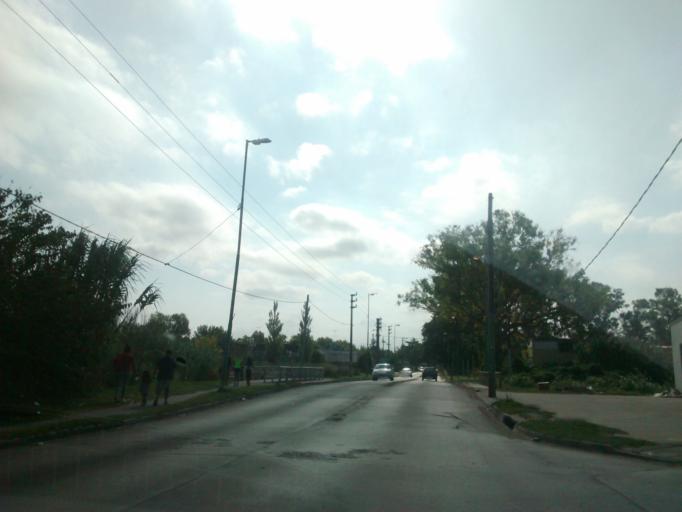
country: AR
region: Buenos Aires
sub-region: Partido de La Plata
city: La Plata
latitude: -34.9472
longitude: -57.9072
